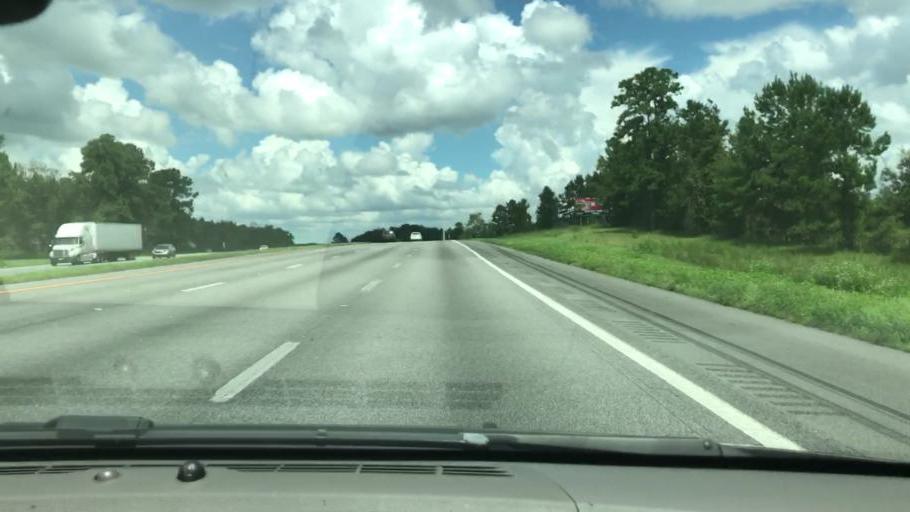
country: US
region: Florida
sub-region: Alachua County
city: High Springs
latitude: 29.8960
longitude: -82.5474
